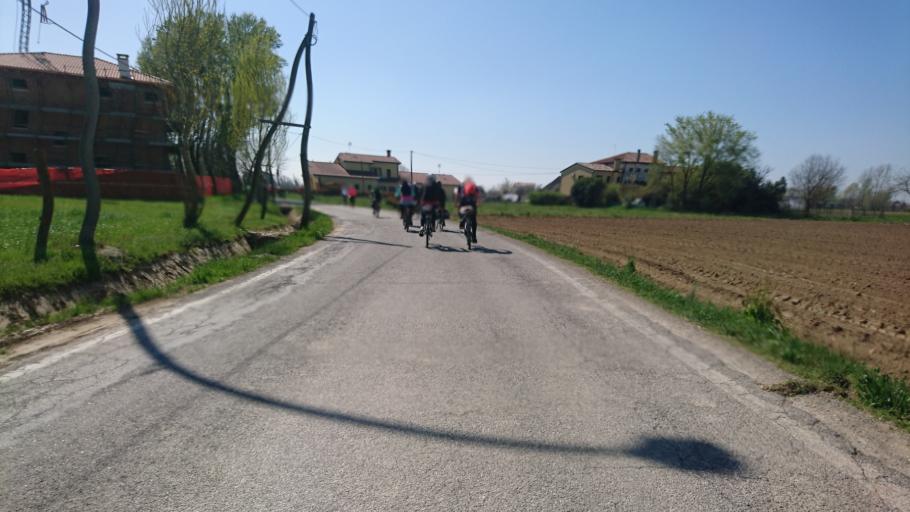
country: IT
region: Veneto
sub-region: Provincia di Padova
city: Cittadella
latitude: 45.6175
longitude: 11.7811
